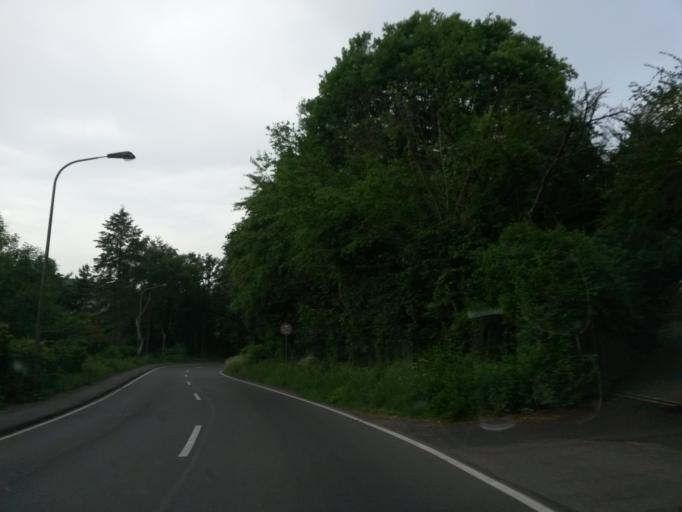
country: DE
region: North Rhine-Westphalia
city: Lohmar
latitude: 50.8573
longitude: 7.2204
